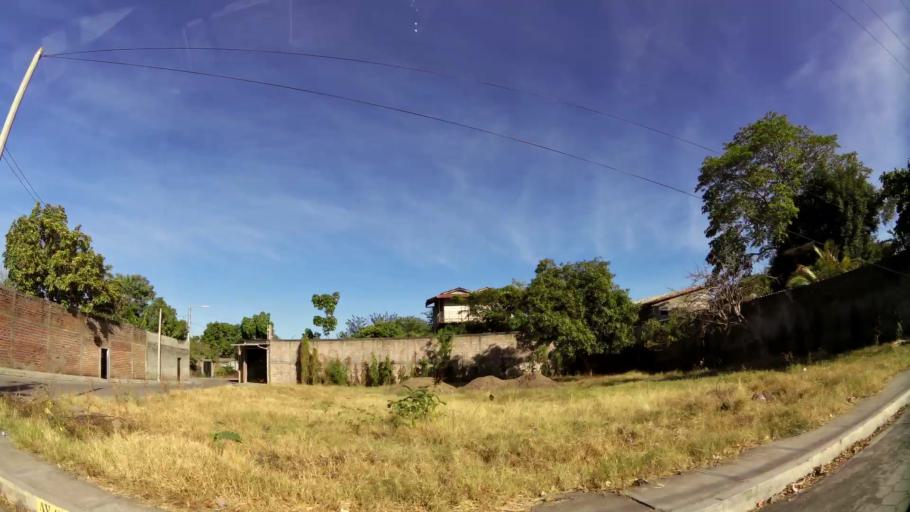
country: SV
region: San Miguel
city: San Miguel
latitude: 13.4679
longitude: -88.1879
